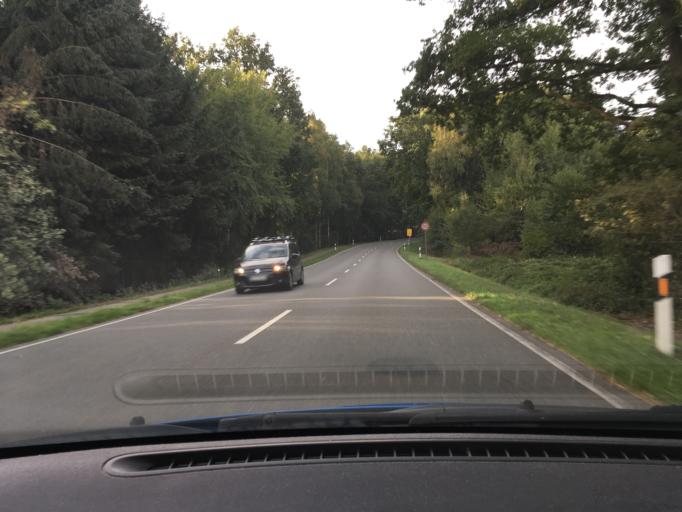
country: DE
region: Lower Saxony
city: Soltau
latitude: 52.9980
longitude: 9.9028
